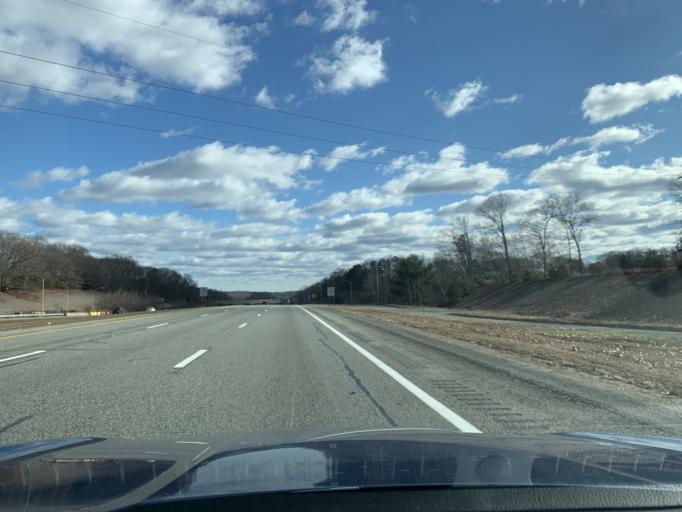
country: US
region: Rhode Island
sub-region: Providence County
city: Cumberland Hill
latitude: 41.9416
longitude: -71.4640
